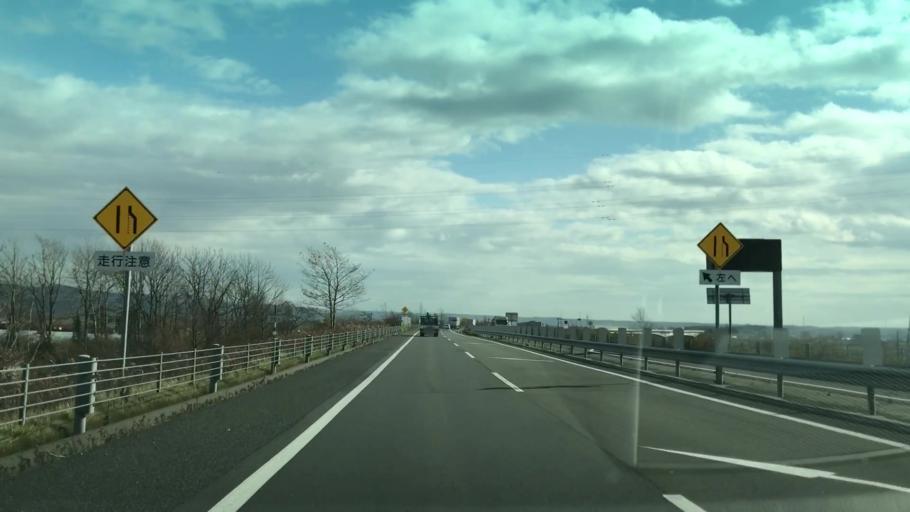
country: JP
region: Hokkaido
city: Tomakomai
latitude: 42.5870
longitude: 141.9358
